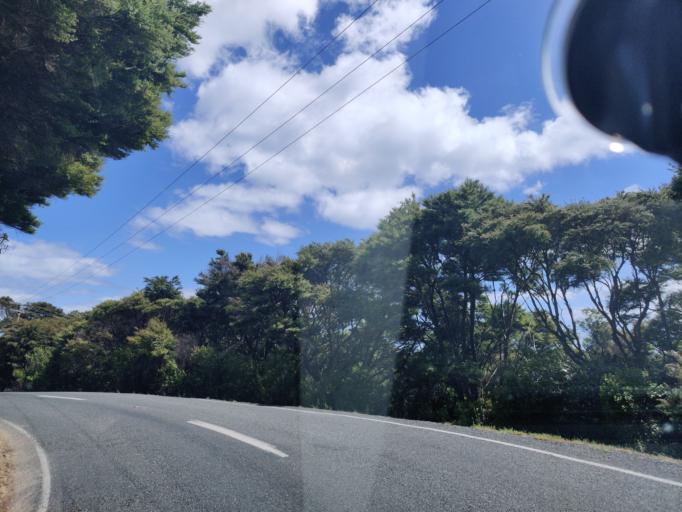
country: NZ
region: Northland
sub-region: Far North District
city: Paihia
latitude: -35.2591
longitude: 174.2451
